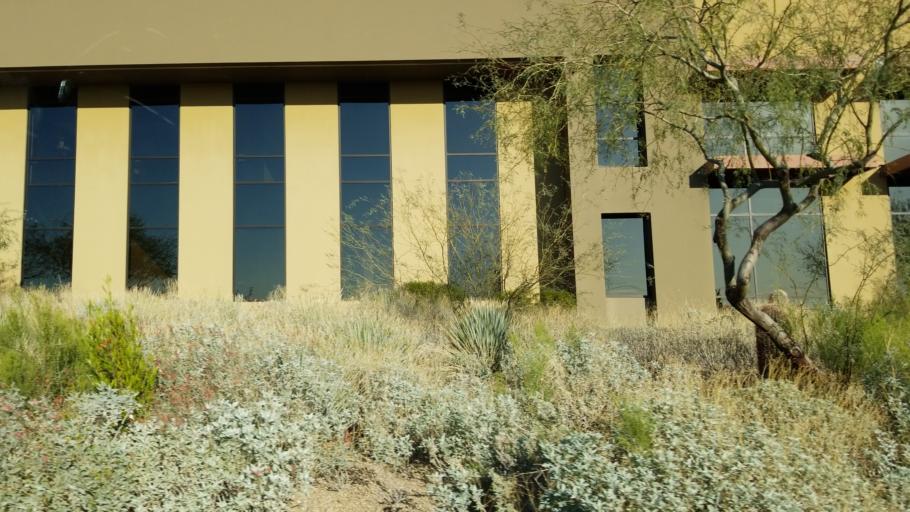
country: US
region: Arizona
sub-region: Maricopa County
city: Paradise Valley
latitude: 33.6573
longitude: -111.8906
